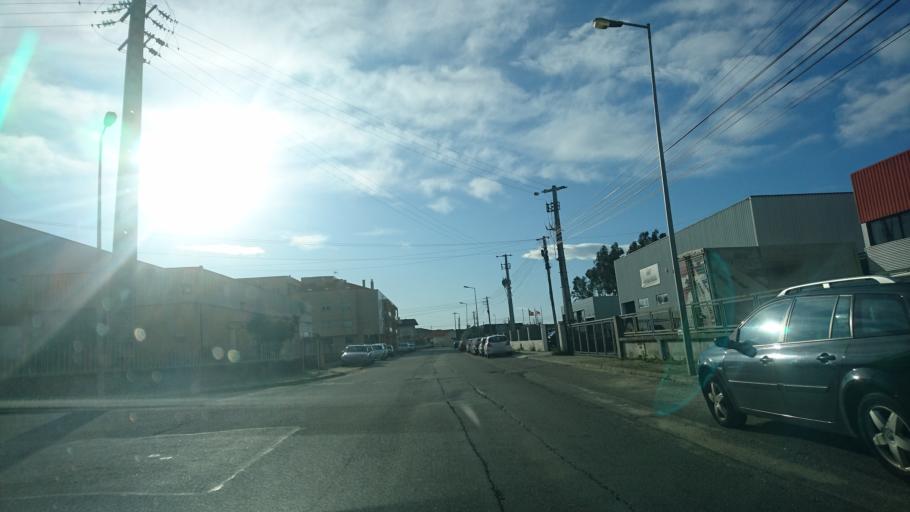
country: PT
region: Aveiro
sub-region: Santa Maria da Feira
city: Pacos de Brandao
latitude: 40.9626
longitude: -8.5997
